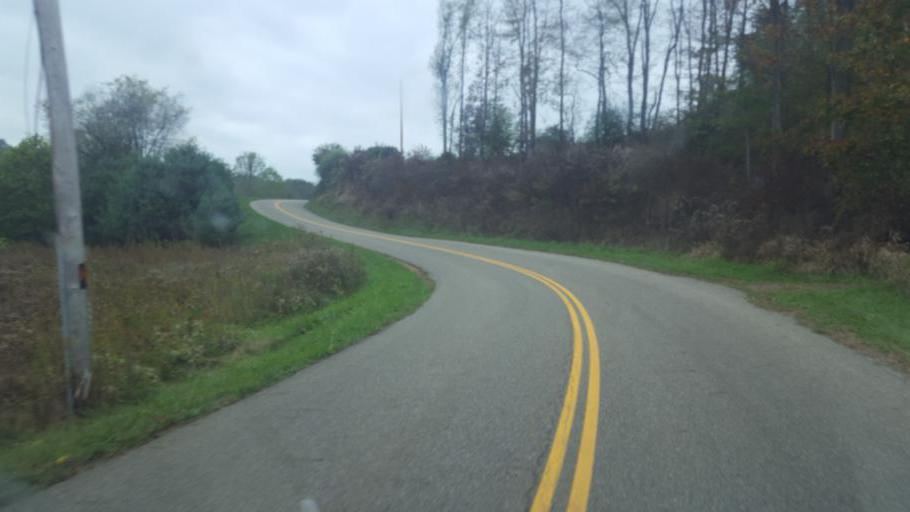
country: US
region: Ohio
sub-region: Carroll County
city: Carrollton
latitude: 40.4797
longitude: -81.0628
